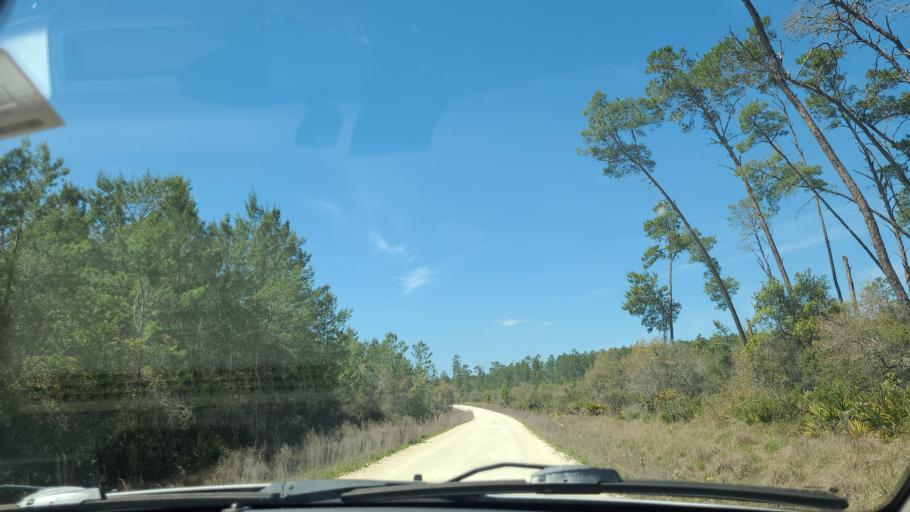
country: US
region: Florida
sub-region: Putnam County
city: Interlachen
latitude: 29.4373
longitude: -81.7621
